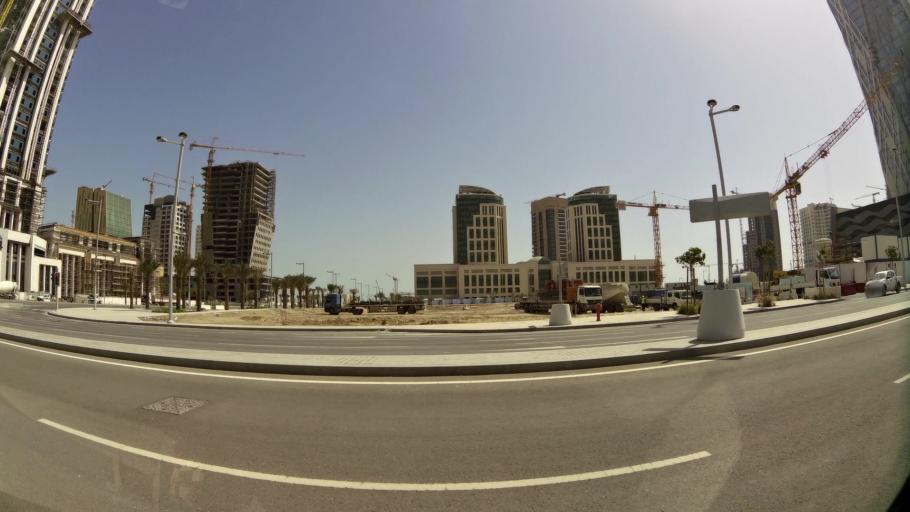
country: QA
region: Baladiyat ad Dawhah
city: Doha
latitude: 25.3929
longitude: 51.5187
